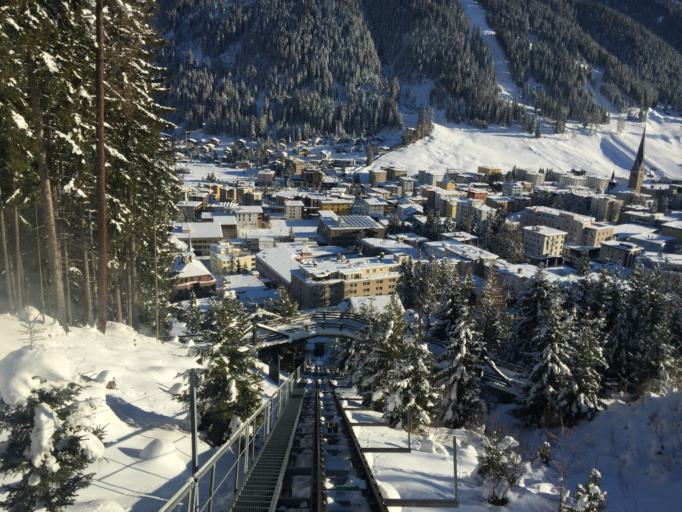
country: CH
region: Grisons
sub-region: Praettigau/Davos District
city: Davos
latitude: 46.7982
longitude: 9.8197
